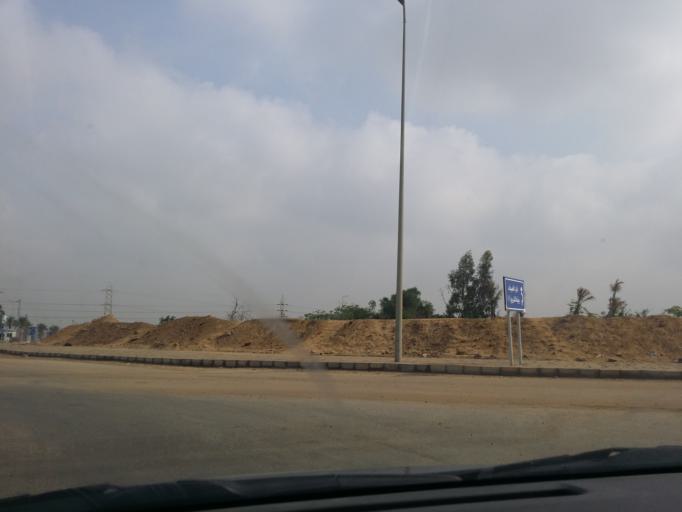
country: EG
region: Muhafazat al Qalyubiyah
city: Al Khankah
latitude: 30.1106
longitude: 31.6314
